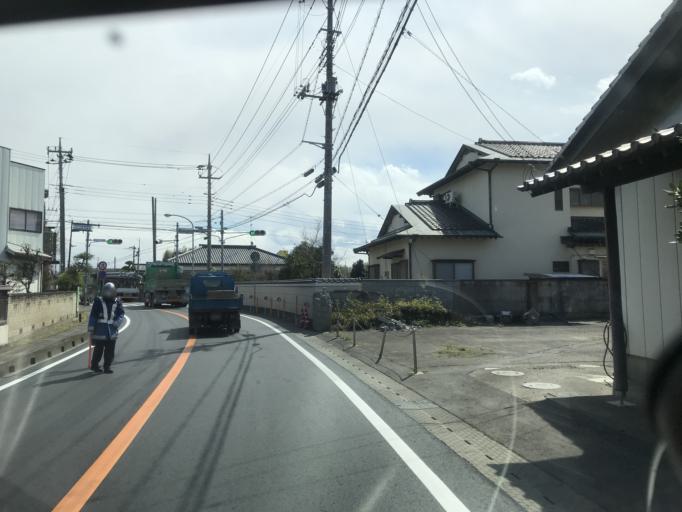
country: JP
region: Ibaraki
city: Yuki
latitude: 36.2580
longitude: 139.9137
